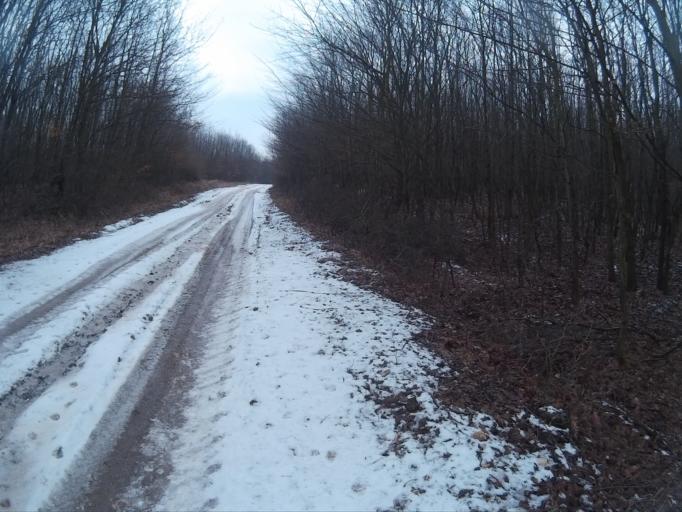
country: HU
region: Komarom-Esztergom
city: Tarjan
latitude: 47.5831
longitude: 18.5262
